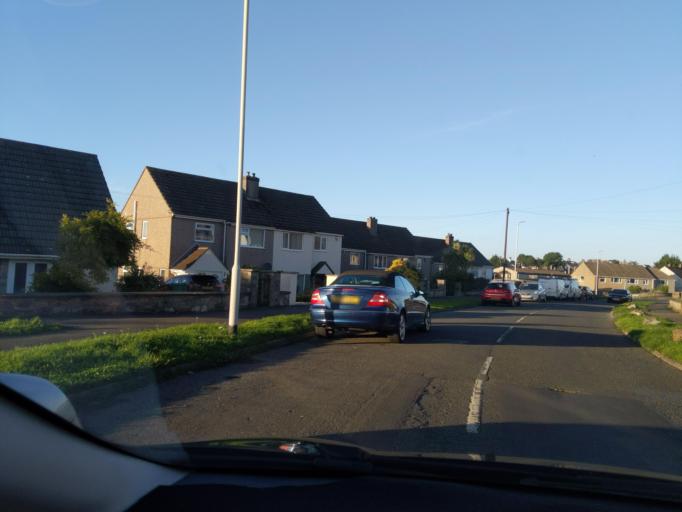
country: GB
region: England
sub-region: Plymouth
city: Plymstock
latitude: 50.3579
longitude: -4.0955
